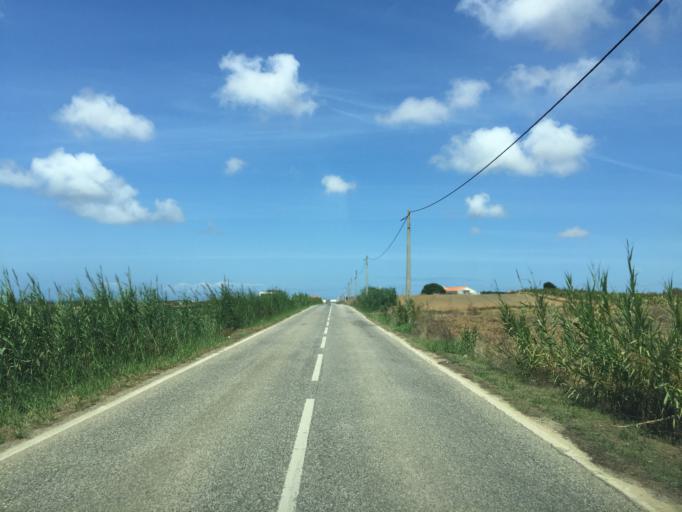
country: PT
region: Lisbon
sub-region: Lourinha
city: Lourinha
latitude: 39.2869
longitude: -9.3048
